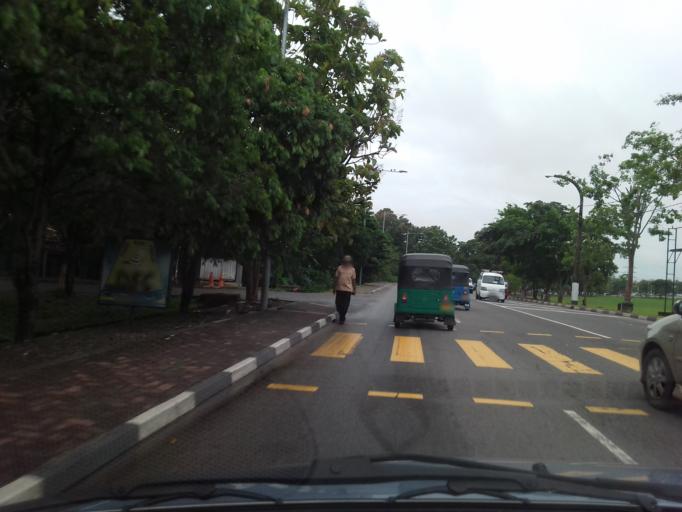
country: LK
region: Western
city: Battaramulla South
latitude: 6.8936
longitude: 79.9181
